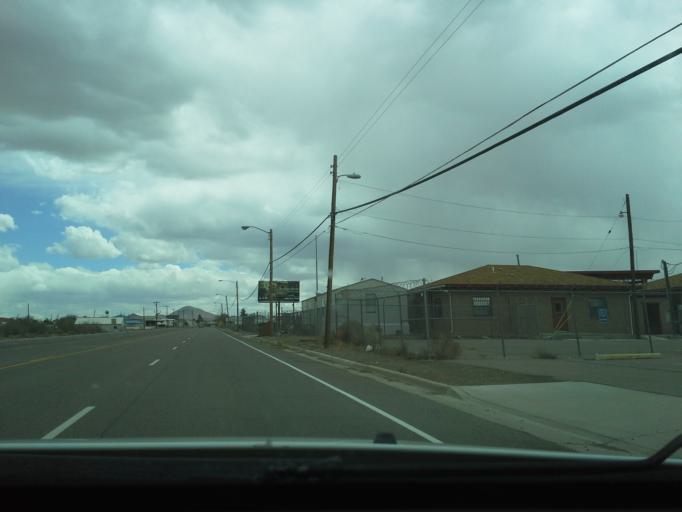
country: US
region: New Mexico
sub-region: Hidalgo County
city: Lordsburg
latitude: 32.3564
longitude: -108.7089
